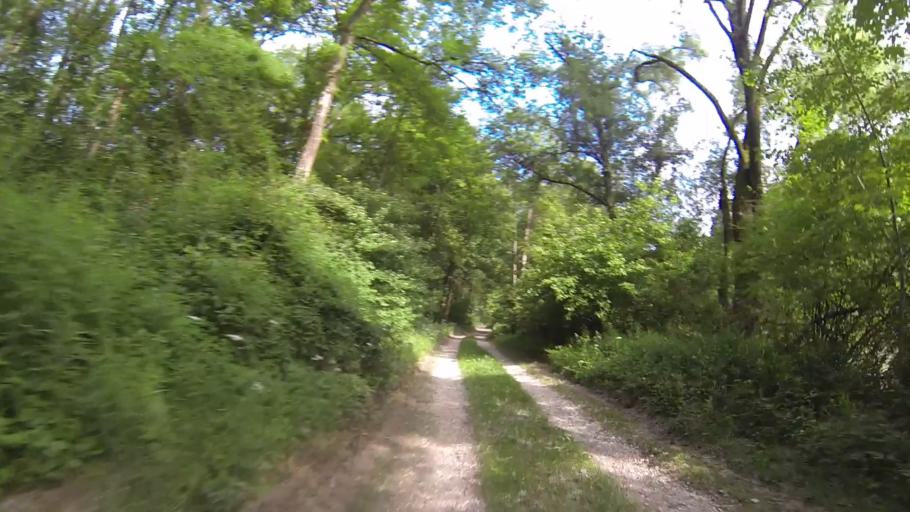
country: DE
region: Bavaria
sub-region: Swabia
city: Senden
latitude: 48.3458
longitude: 10.0060
